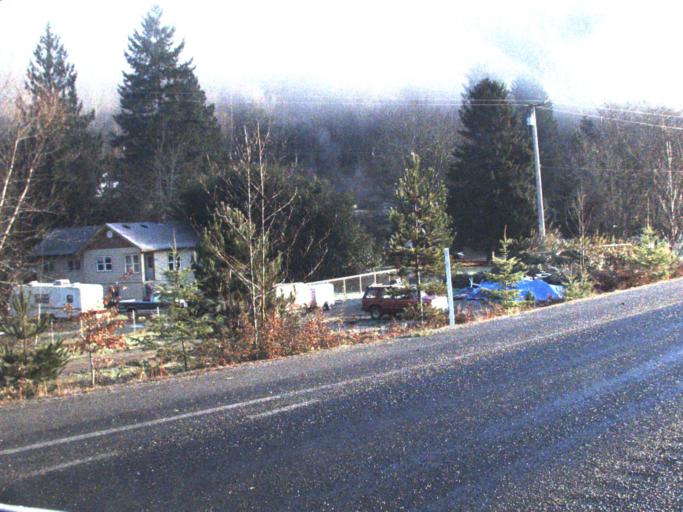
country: US
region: Washington
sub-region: Snohomish County
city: Darrington
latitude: 48.5358
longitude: -121.7378
